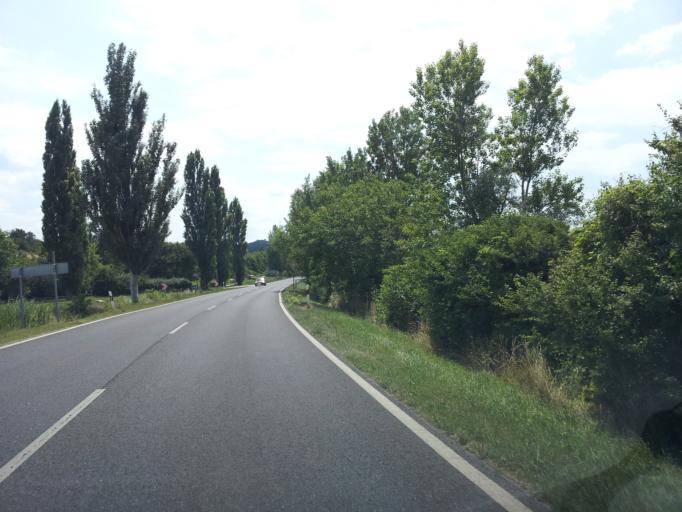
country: HU
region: Veszprem
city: Tihany
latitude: 46.9264
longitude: 17.8596
